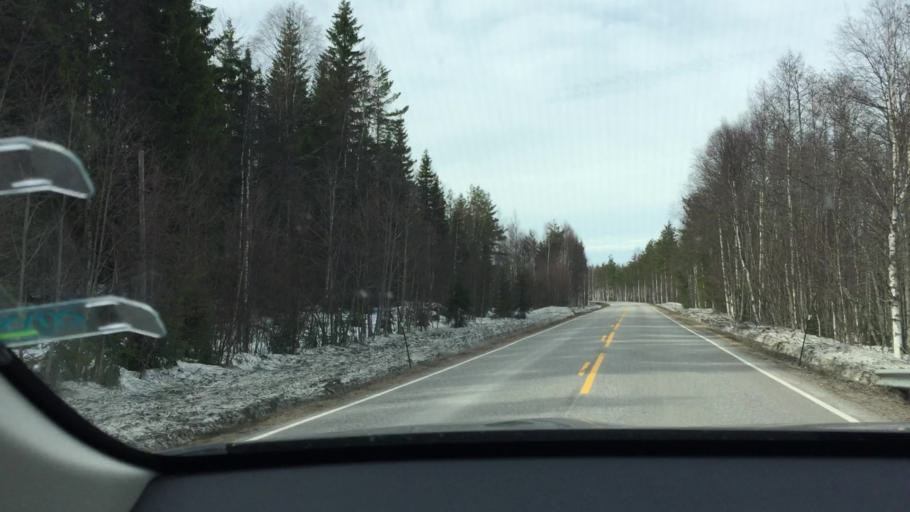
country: NO
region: Hedmark
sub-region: Trysil
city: Innbygda
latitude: 61.0707
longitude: 12.5786
